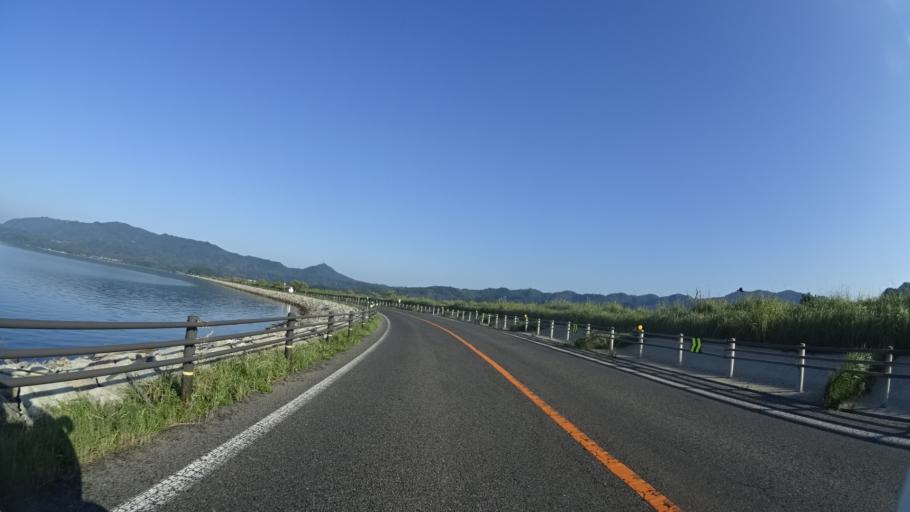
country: JP
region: Shimane
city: Sakaiminato
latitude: 35.5235
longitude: 133.1806
